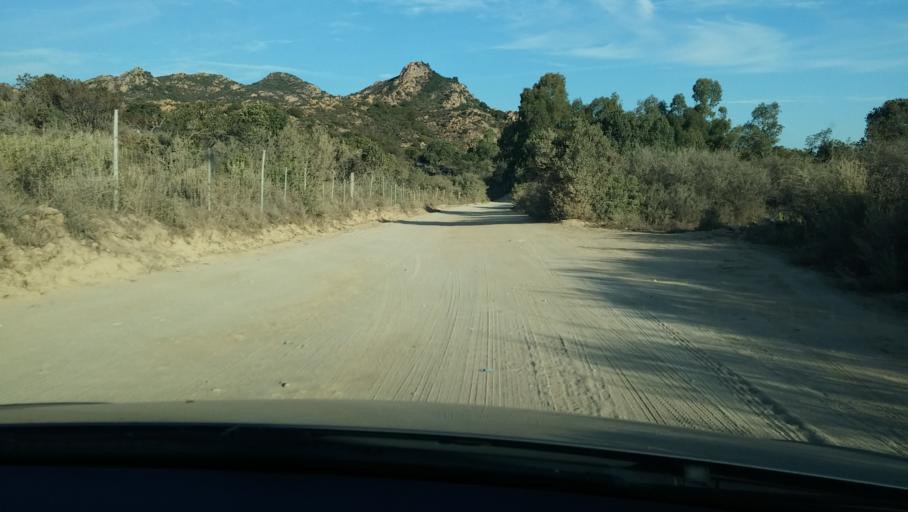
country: IT
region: Sardinia
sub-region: Provincia di Nuoro
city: La Caletta
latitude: 40.4832
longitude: 9.8031
